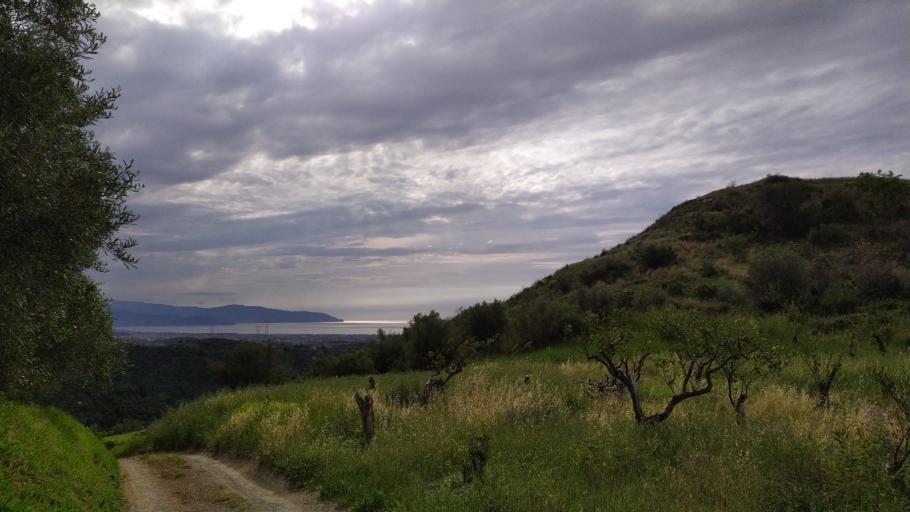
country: IT
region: Sicily
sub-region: Messina
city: Pace del Mela
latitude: 38.1611
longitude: 15.2947
